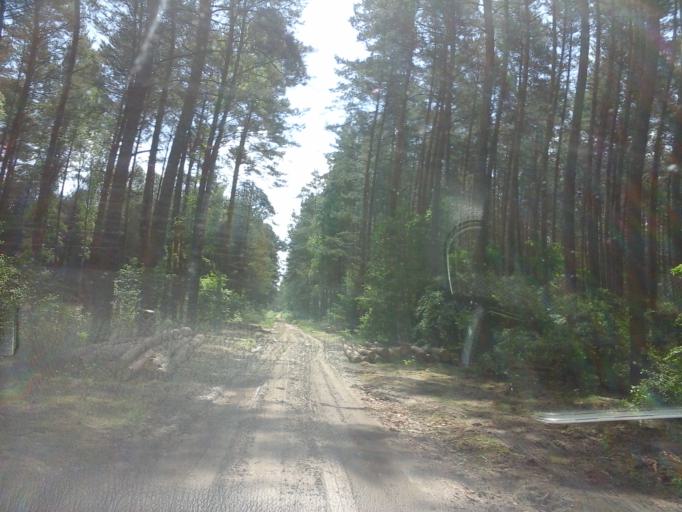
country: PL
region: West Pomeranian Voivodeship
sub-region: Powiat choszczenski
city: Bierzwnik
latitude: 53.1290
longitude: 15.6639
